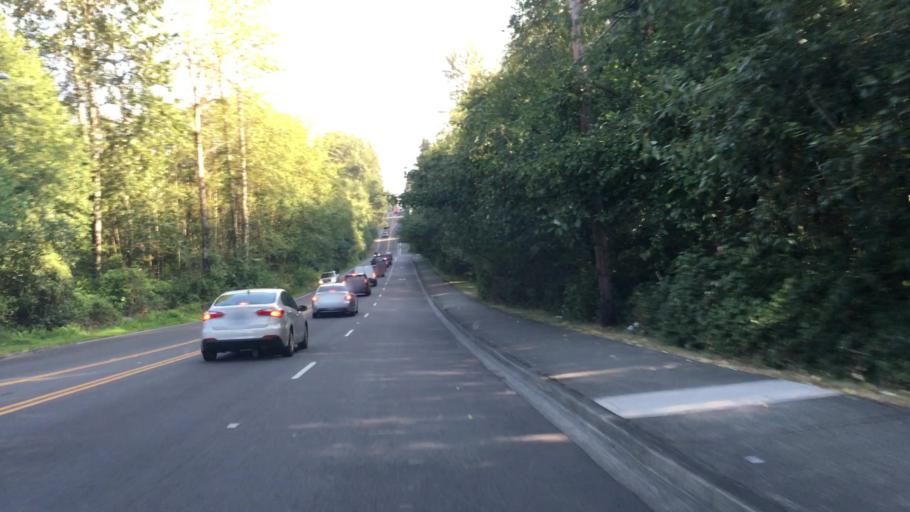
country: US
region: Washington
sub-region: Pierce County
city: Fife Heights
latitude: 47.2884
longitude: -122.3347
